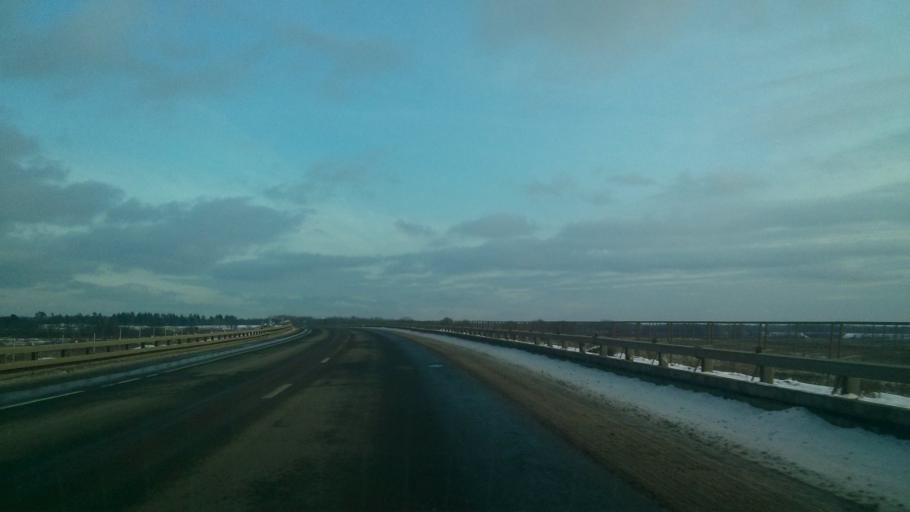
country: RU
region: Nizjnij Novgorod
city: Navashino
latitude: 55.5875
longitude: 42.1281
